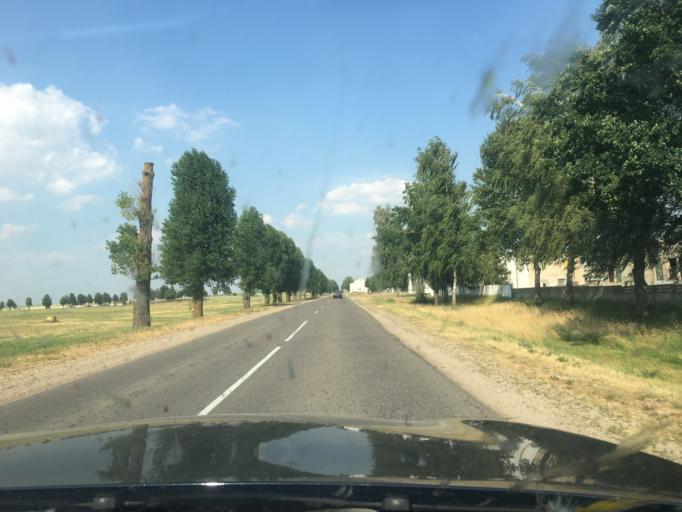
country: BY
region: Grodnenskaya
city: Svislach
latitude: 53.0399
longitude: 24.0781
